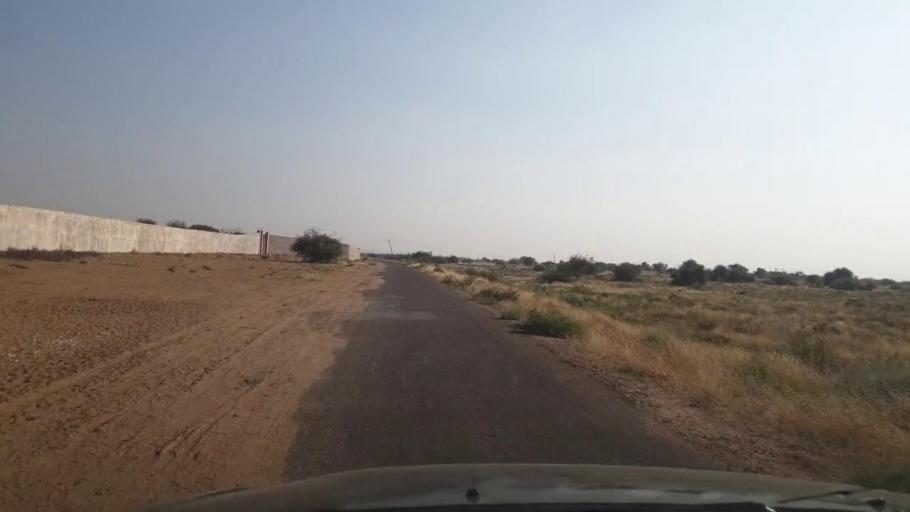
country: PK
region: Sindh
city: Jamshoro
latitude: 25.3486
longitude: 67.8378
